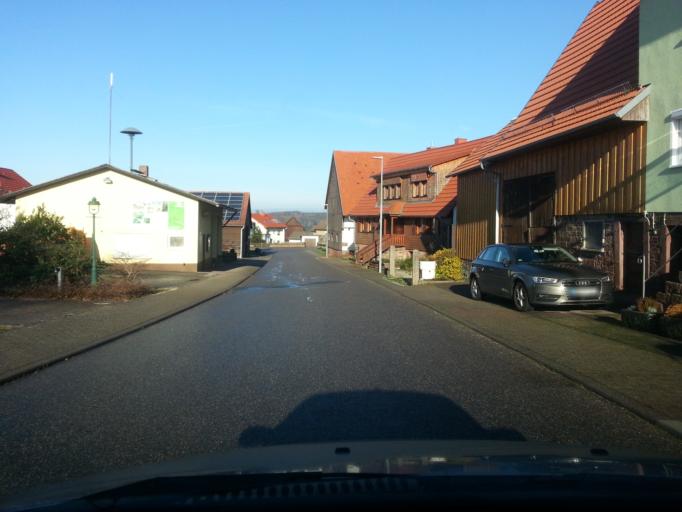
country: DE
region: Baden-Wuerttemberg
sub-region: Karlsruhe Region
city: Zwingenberg
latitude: 49.4646
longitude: 9.0815
